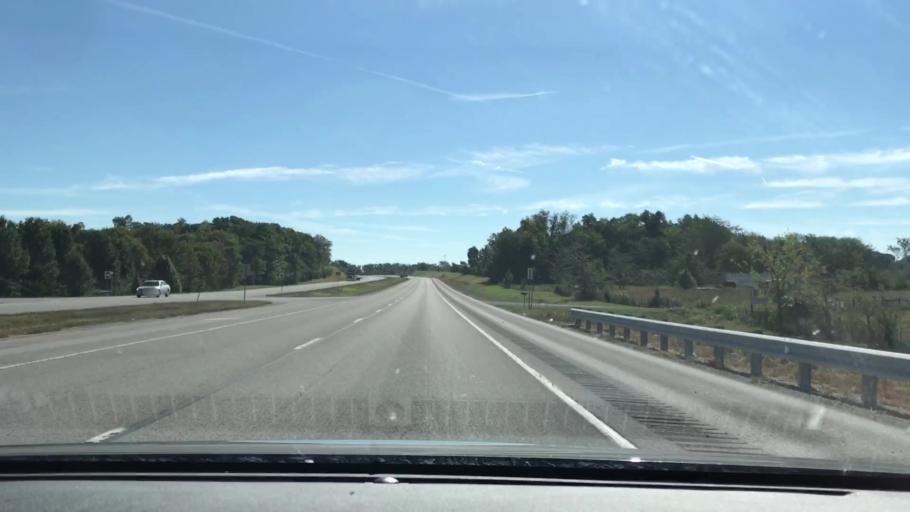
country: US
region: Kentucky
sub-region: Todd County
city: Elkton
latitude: 36.8303
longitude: -87.2271
